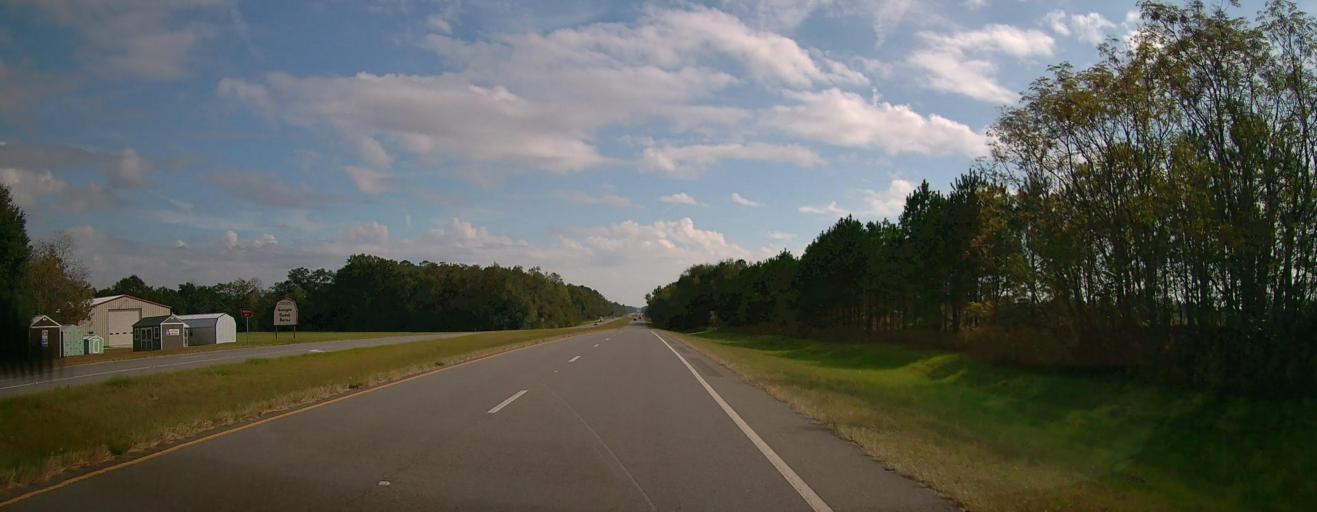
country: US
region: Georgia
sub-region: Thomas County
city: Meigs
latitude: 31.0091
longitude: -84.0523
